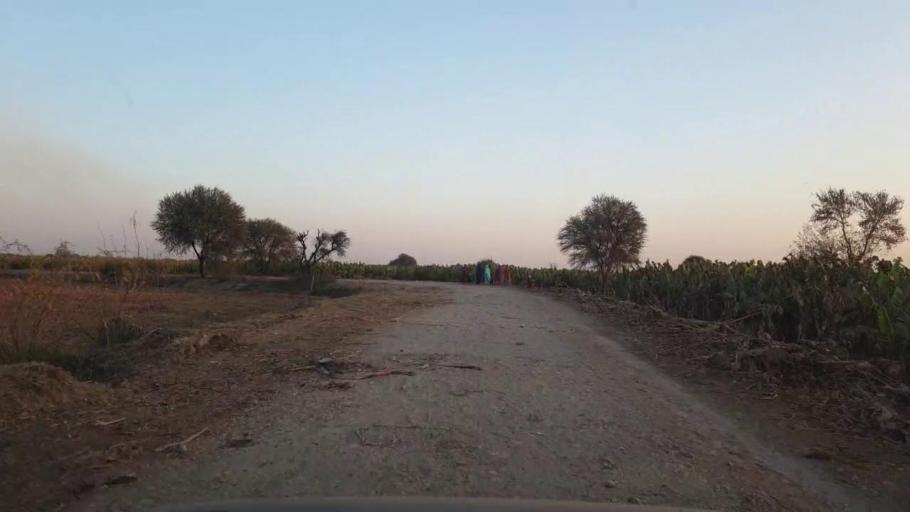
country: PK
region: Sindh
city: Chambar
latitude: 25.3556
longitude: 68.7382
